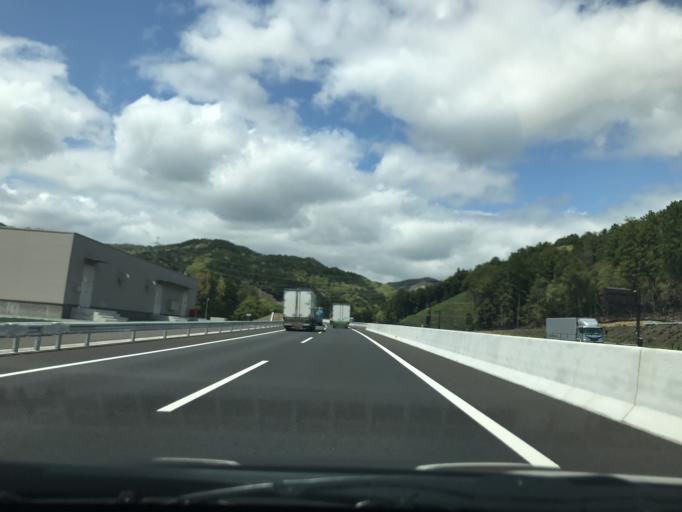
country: JP
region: Osaka
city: Takatsuki
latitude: 34.8977
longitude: 135.6056
